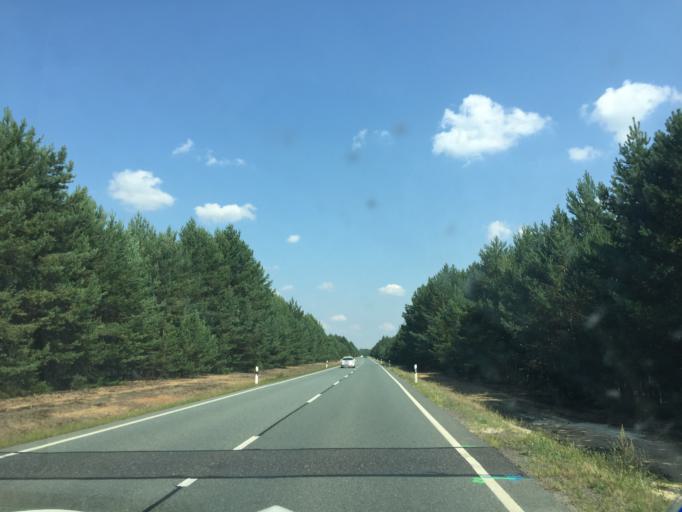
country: DE
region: Saxony
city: Uhyst
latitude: 51.3784
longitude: 14.4932
